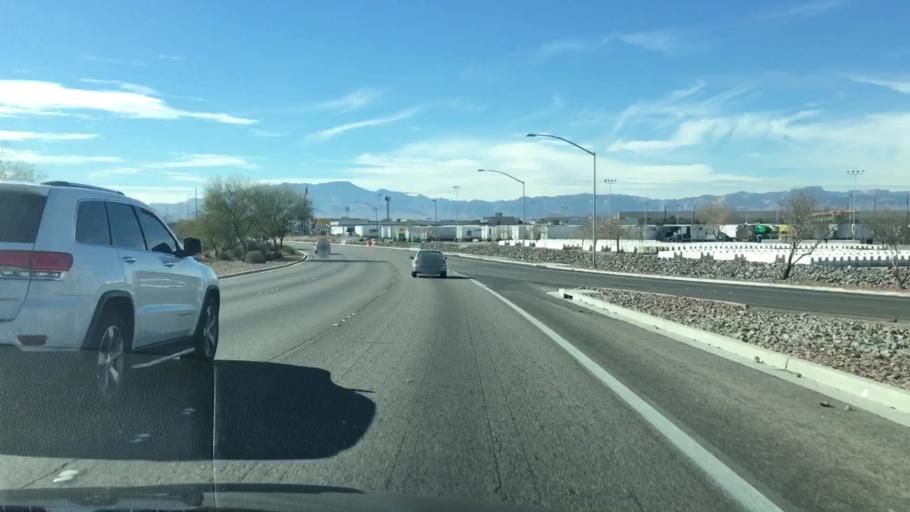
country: US
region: Nevada
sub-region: Clark County
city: Enterprise
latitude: 36.0436
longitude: -115.1830
